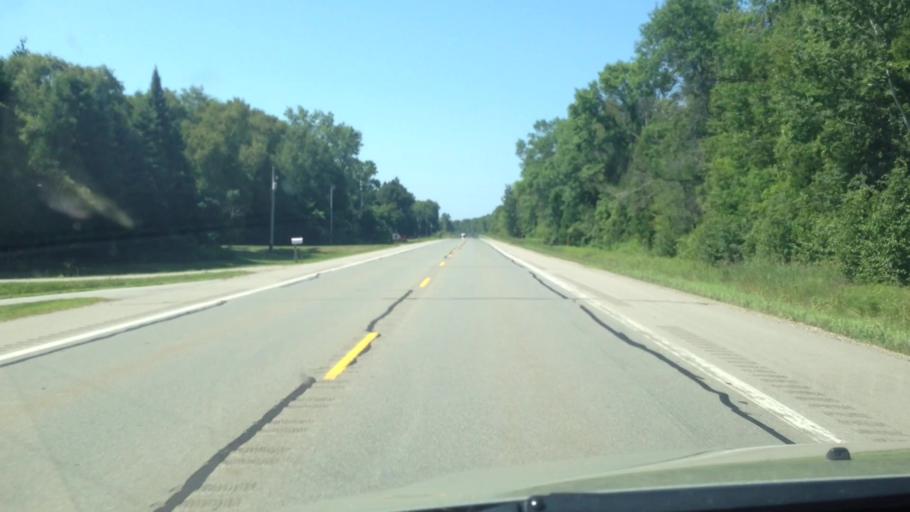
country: US
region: Michigan
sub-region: Menominee County
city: Menominee
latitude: 45.2372
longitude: -87.5022
